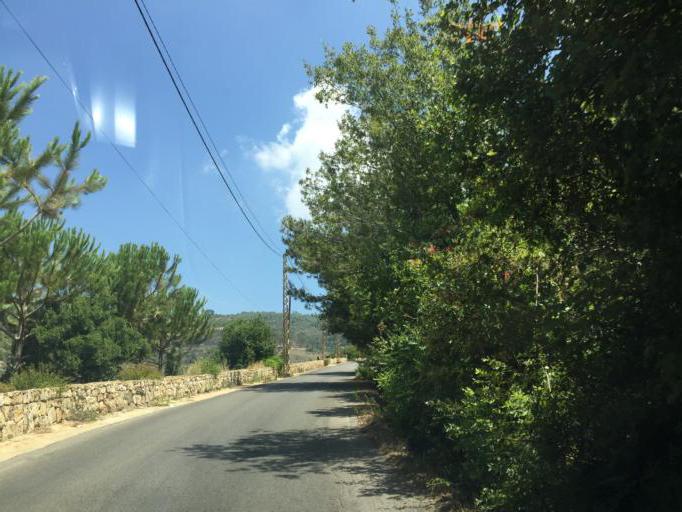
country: LB
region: Mont-Liban
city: Beit ed Dine
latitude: 33.6943
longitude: 35.5743
